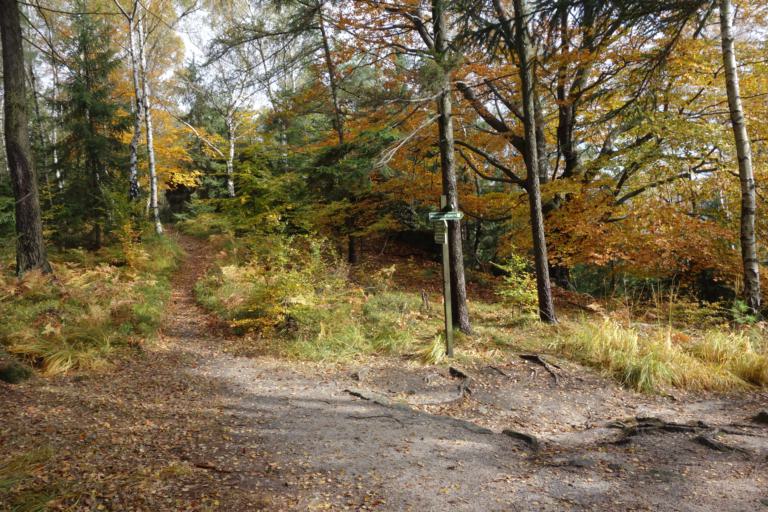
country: DE
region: Saxony
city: Kurort Oybin
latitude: 50.8474
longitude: 14.7355
